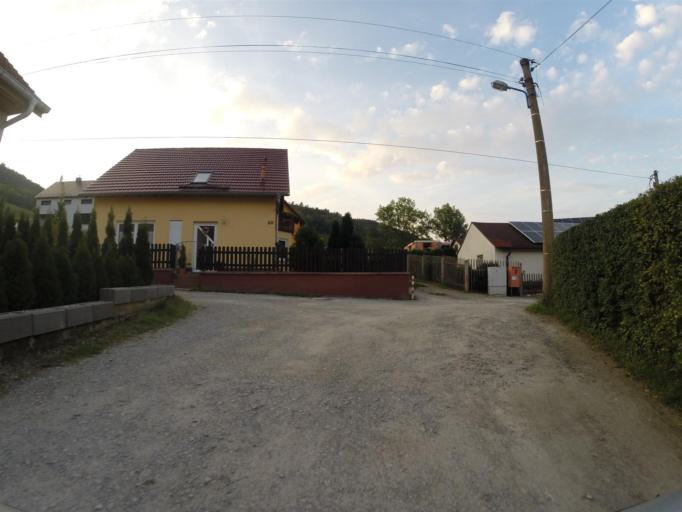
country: DE
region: Thuringia
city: Rothenstein
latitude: 50.8777
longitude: 11.5870
